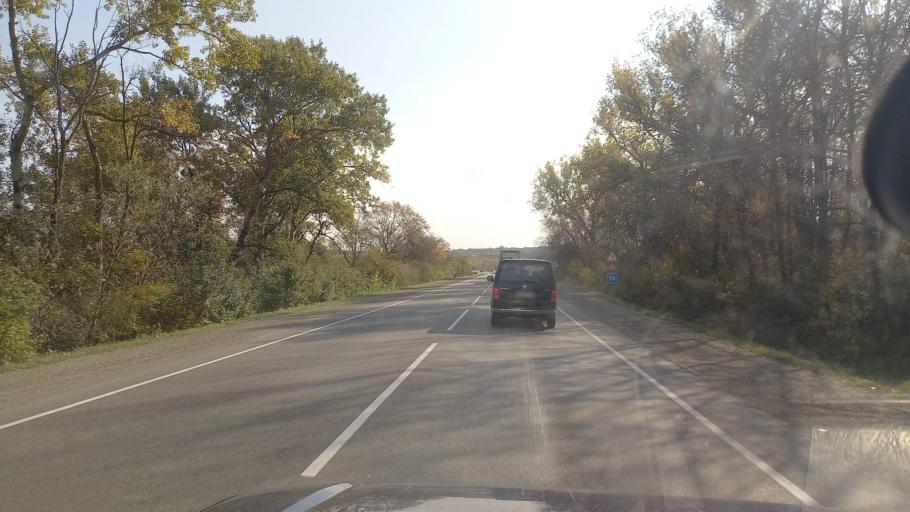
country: RU
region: Krasnodarskiy
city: Abinsk
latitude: 44.8421
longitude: 38.1588
